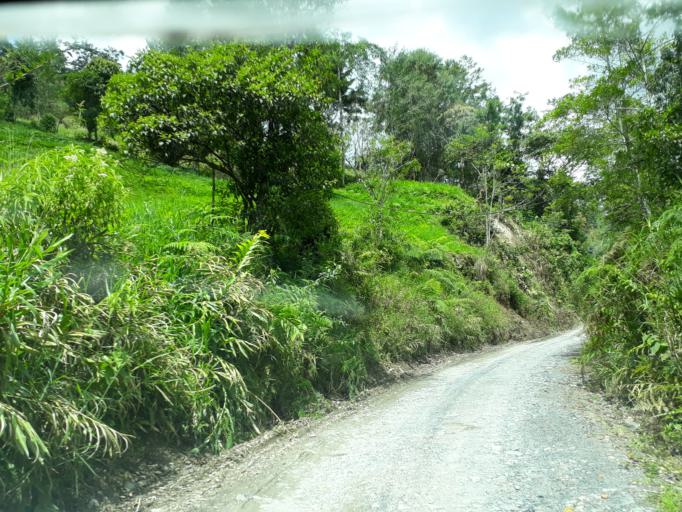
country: CO
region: Cundinamarca
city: Topaipi
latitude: 5.3475
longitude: -74.1916
